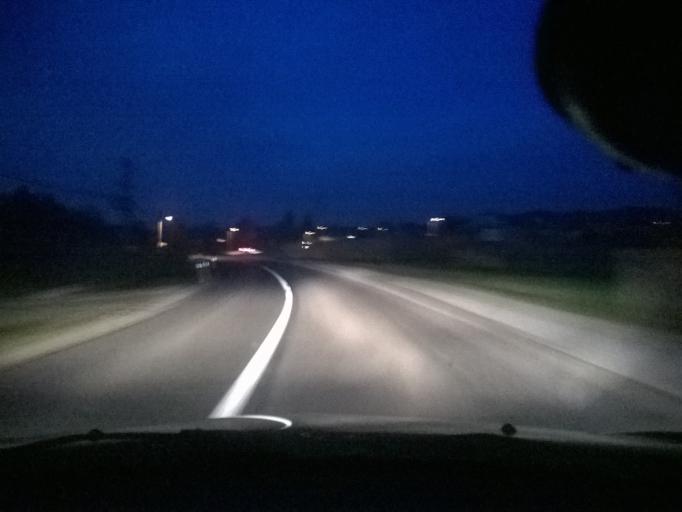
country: HR
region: Krapinsko-Zagorska
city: Zabok
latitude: 46.0497
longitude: 15.9261
